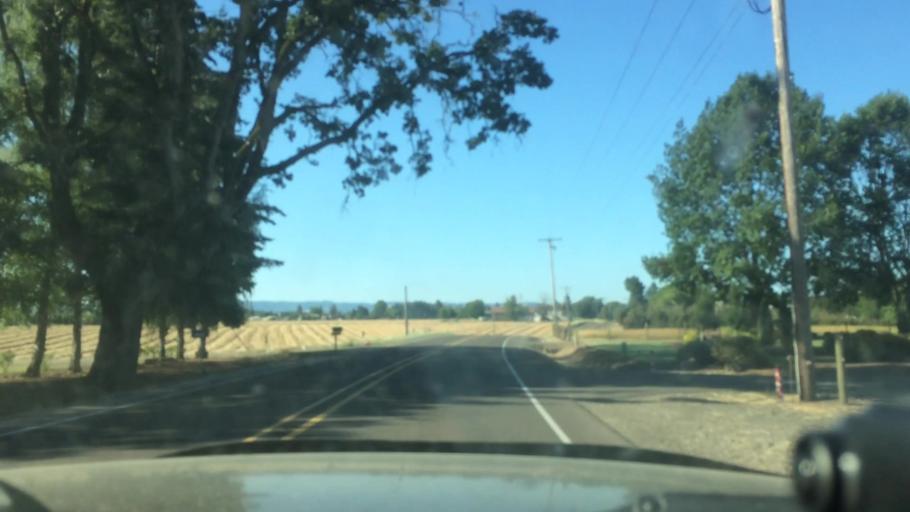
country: US
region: Oregon
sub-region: Yamhill County
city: Dundee
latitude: 45.2016
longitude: -122.9830
